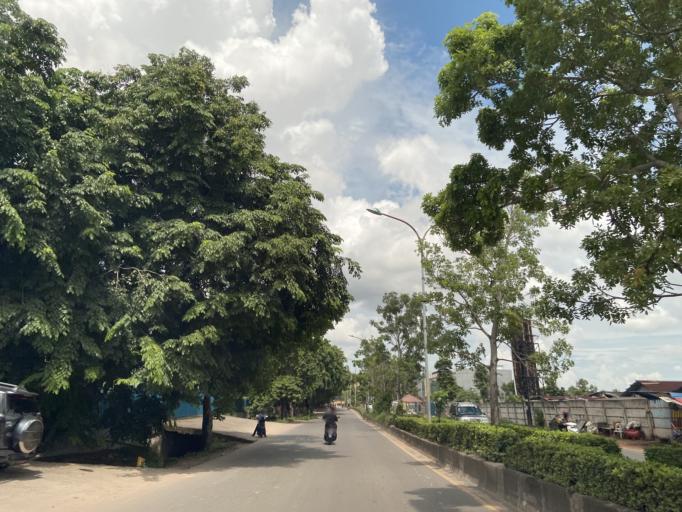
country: SG
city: Singapore
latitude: 1.1453
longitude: 104.0034
